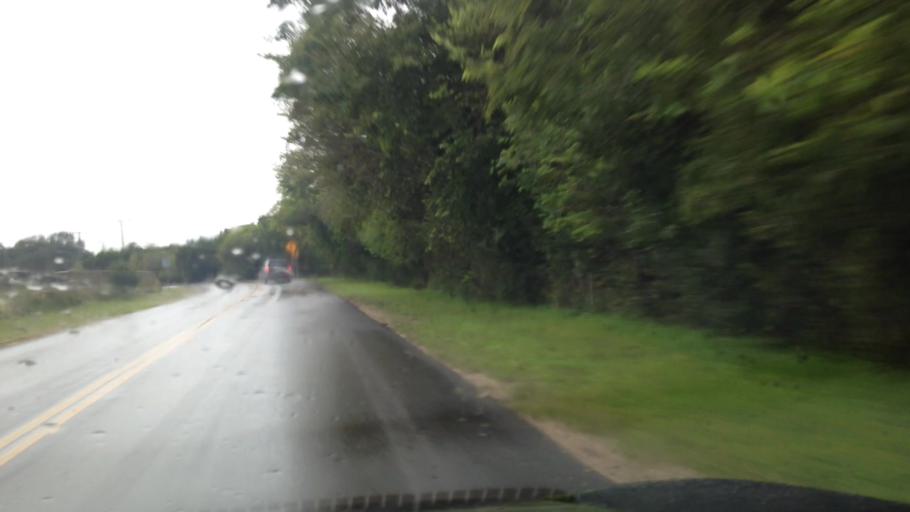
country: US
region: Texas
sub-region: Bexar County
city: Cross Mountain
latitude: 29.6343
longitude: -98.6024
